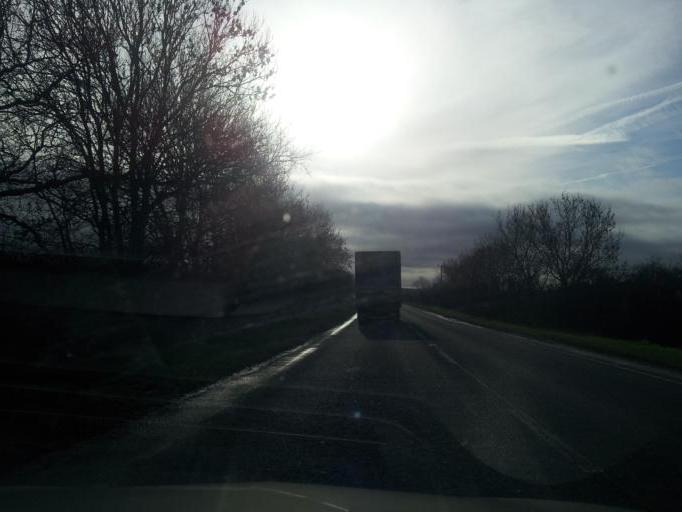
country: GB
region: England
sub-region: District of Rutland
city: Ketton
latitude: 52.6046
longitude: -0.5361
